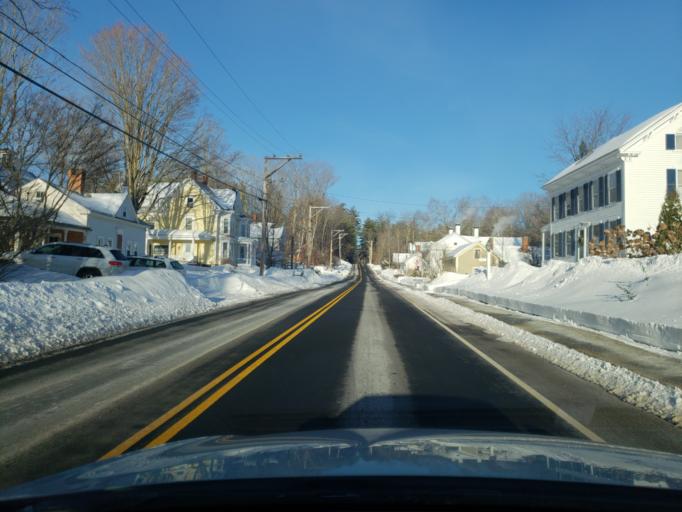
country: US
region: New Hampshire
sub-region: Hillsborough County
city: Greenfield
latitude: 42.9909
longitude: -71.8161
